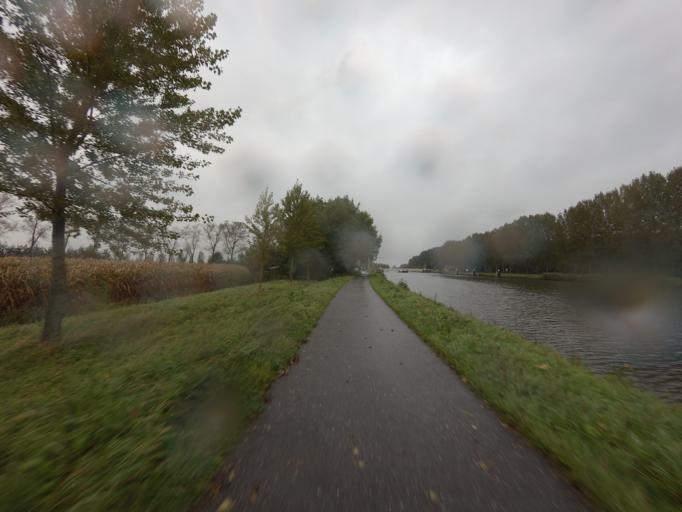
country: NL
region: Utrecht
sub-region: Gemeente Vianen
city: Vianen
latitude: 51.9675
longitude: 5.0694
